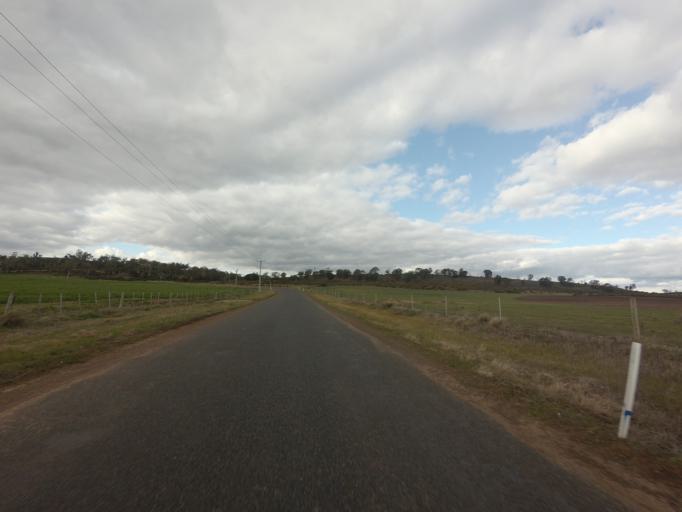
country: AU
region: Tasmania
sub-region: Northern Midlands
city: Evandale
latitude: -41.8995
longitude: 147.4050
